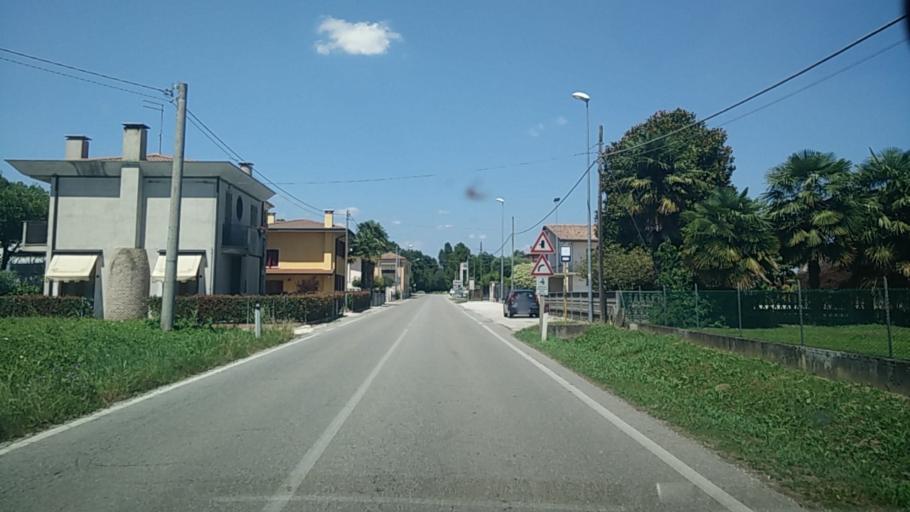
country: IT
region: Veneto
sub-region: Provincia di Padova
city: Tombolo
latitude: 45.6364
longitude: 11.8252
